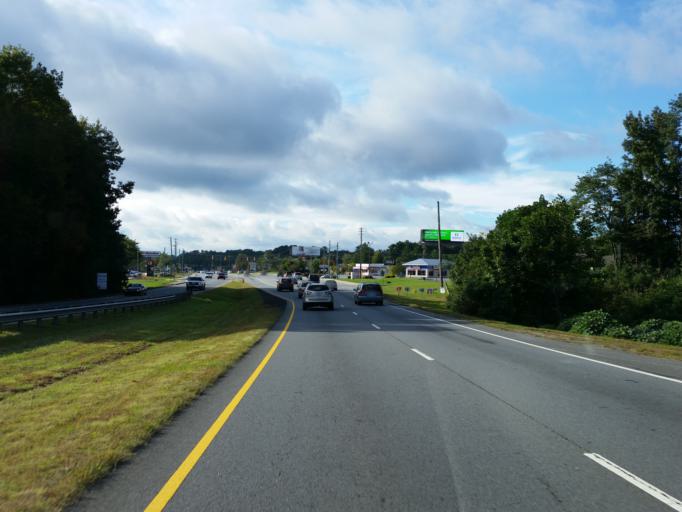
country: US
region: Georgia
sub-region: Cobb County
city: Kennesaw
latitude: 34.0192
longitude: -84.6196
